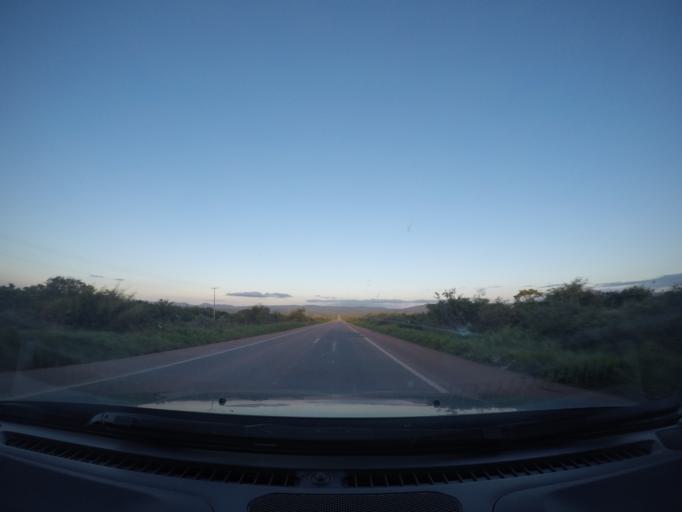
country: BR
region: Bahia
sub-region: Seabra
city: Seabra
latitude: -12.4092
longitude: -41.9663
